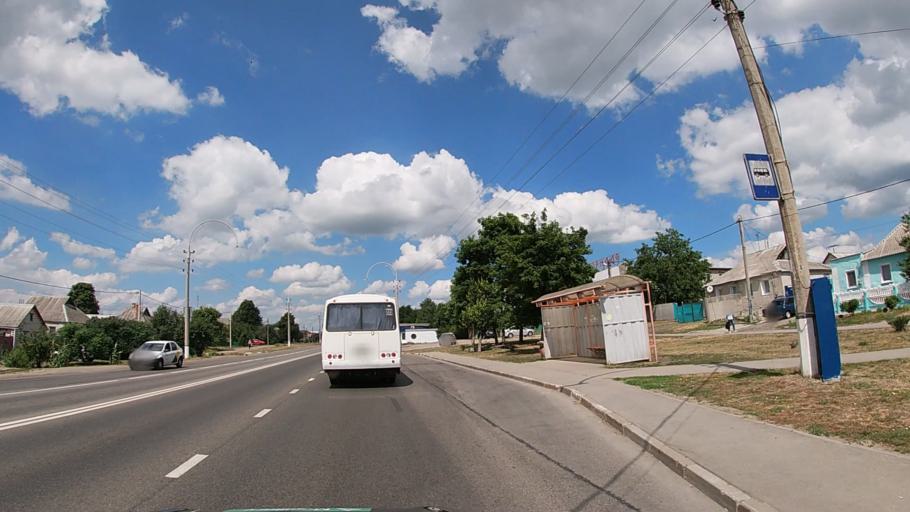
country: RU
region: Belgorod
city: Severnyy
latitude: 50.6252
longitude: 36.4991
